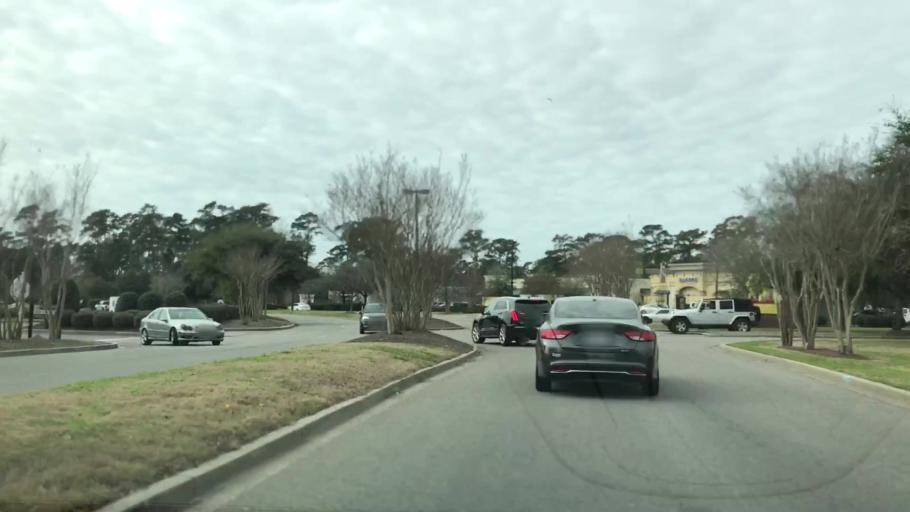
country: US
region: South Carolina
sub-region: Horry County
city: Myrtle Beach
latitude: 33.7263
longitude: -78.8694
